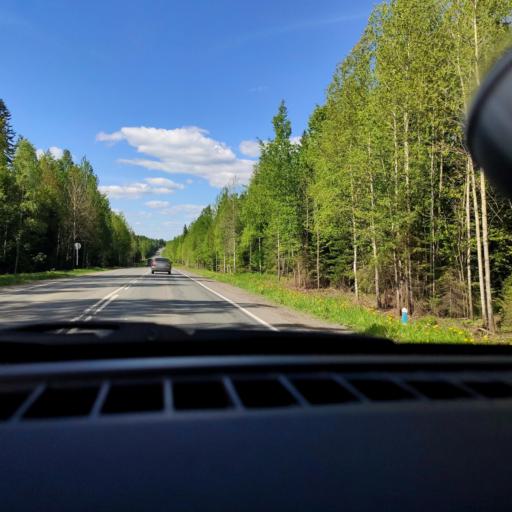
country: RU
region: Perm
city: Perm
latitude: 58.2293
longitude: 56.1626
